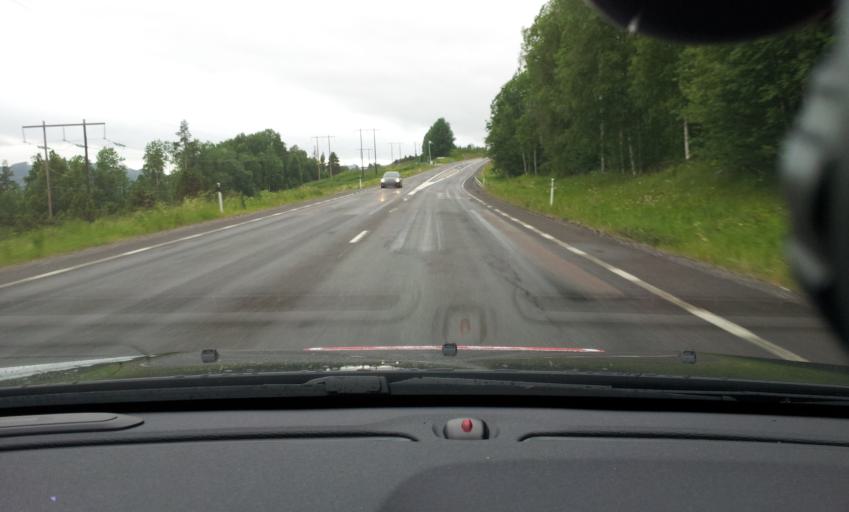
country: SE
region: Jaemtland
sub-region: Ragunda Kommun
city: Hammarstrand
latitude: 63.0521
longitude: 16.5271
